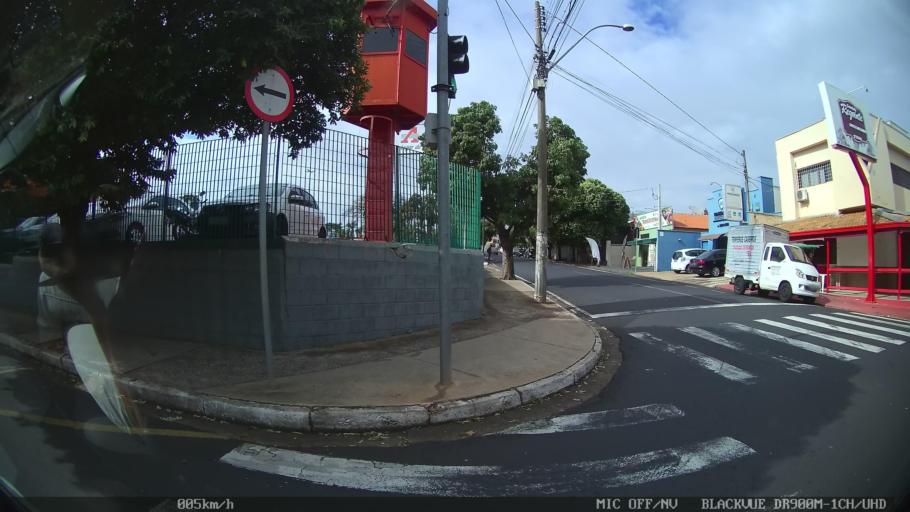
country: BR
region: Sao Paulo
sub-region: Sao Jose Do Rio Preto
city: Sao Jose do Rio Preto
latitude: -20.8187
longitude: -49.3742
